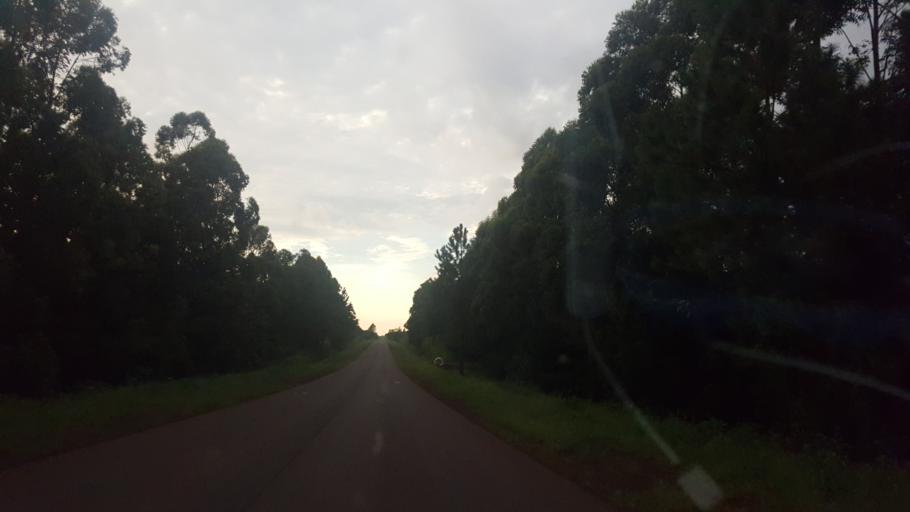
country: AR
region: Misiones
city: Dos de Mayo
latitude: -26.9511
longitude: -54.7148
